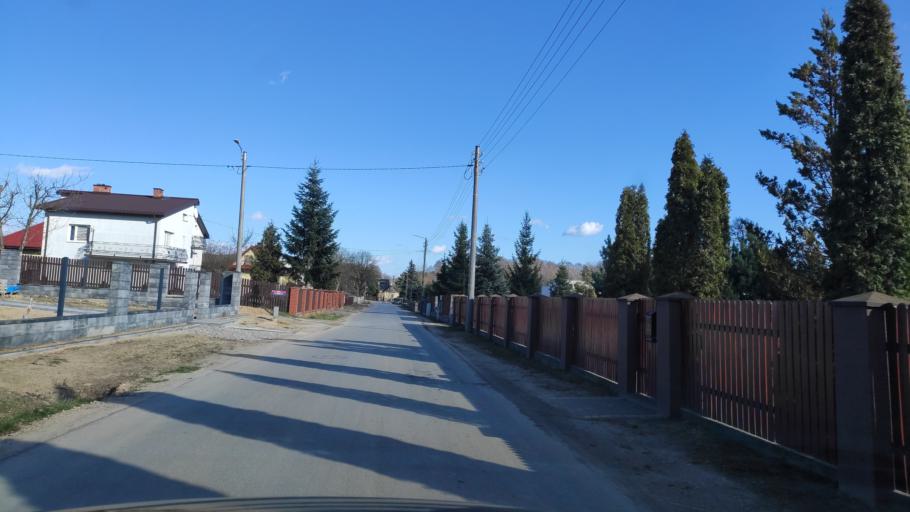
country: PL
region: Masovian Voivodeship
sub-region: Powiat radomski
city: Jedlnia-Letnisko
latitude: 51.4394
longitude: 21.3028
